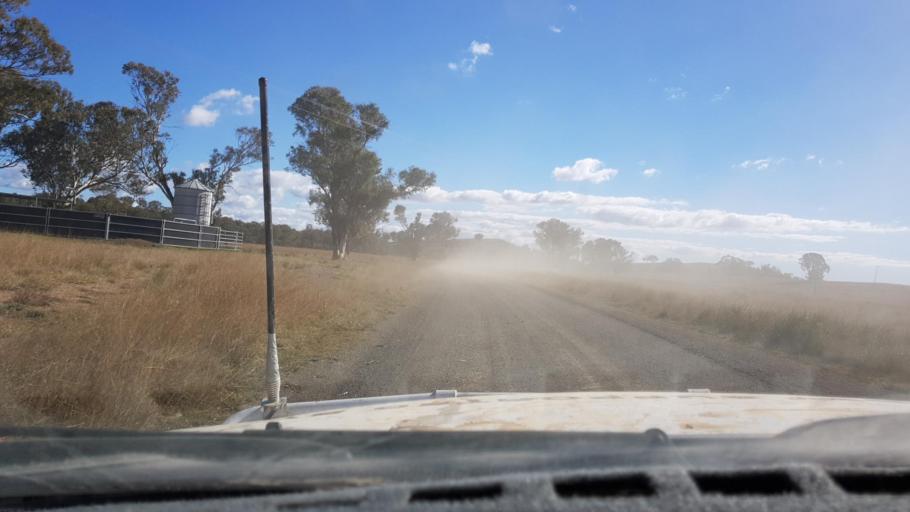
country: AU
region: New South Wales
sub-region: Narrabri
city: Blair Athol
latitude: -30.4902
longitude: 150.4413
